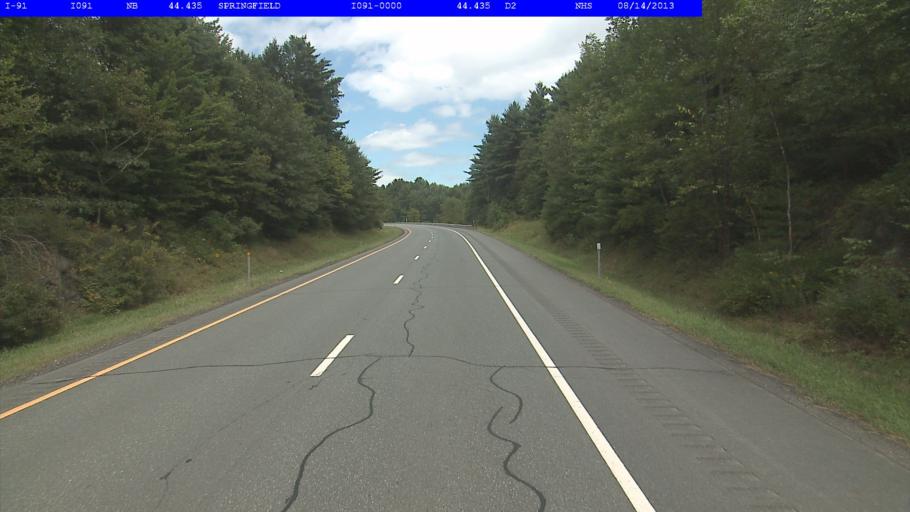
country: US
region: Vermont
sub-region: Windsor County
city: Springfield
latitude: 43.3045
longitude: -72.4232
